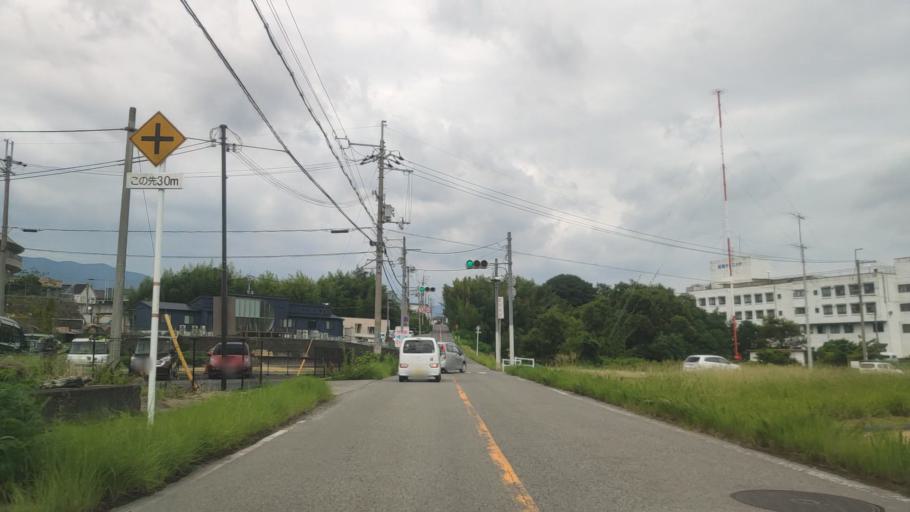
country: JP
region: Wakayama
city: Hashimoto
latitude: 34.3050
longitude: 135.5803
